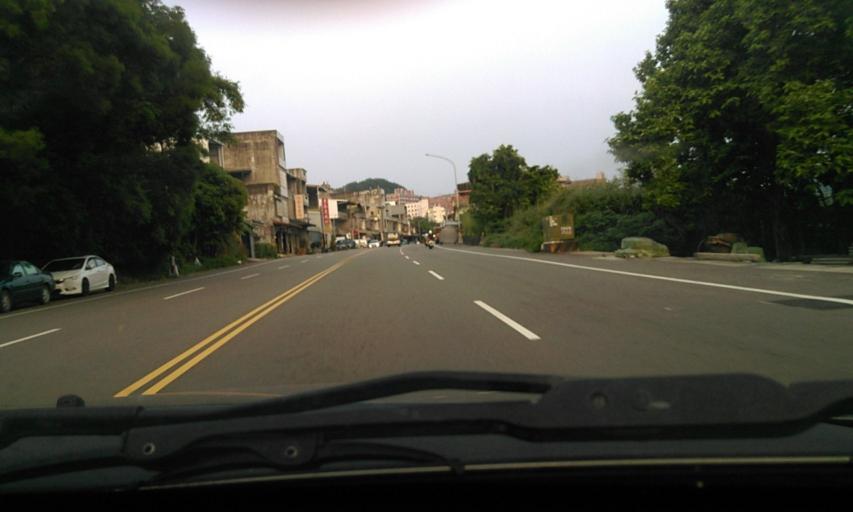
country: TW
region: Taiwan
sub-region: Hsinchu
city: Hsinchu
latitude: 24.6848
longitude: 120.9610
